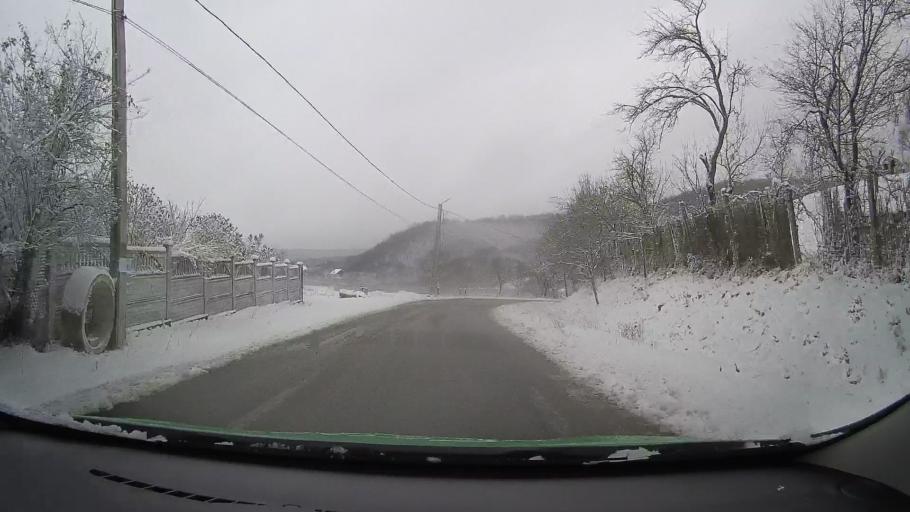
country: RO
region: Hunedoara
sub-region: Municipiul Deva
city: Deva
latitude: 45.8621
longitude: 22.8835
